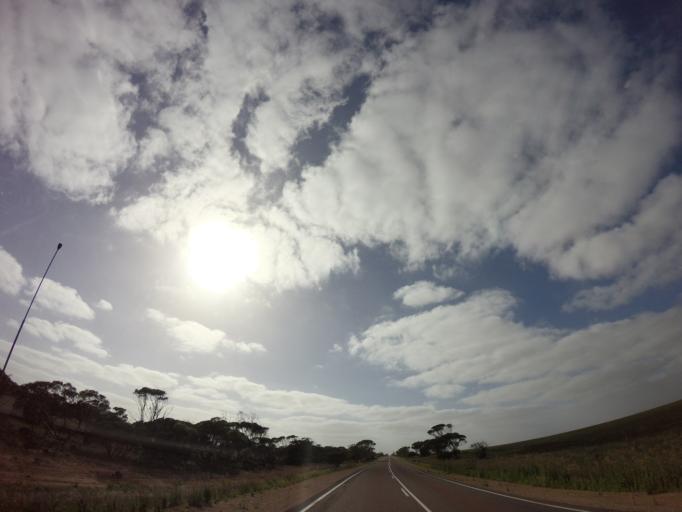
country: AU
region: South Australia
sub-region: Streaky Bay
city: Streaky Bay
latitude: -32.2835
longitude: 134.2271
